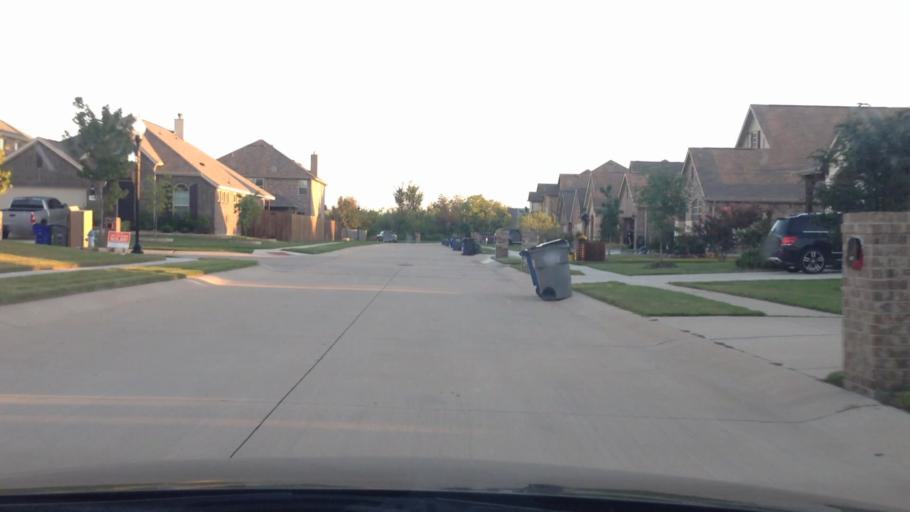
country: US
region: Texas
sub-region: Denton County
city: Little Elm
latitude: 33.1349
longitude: -96.9365
